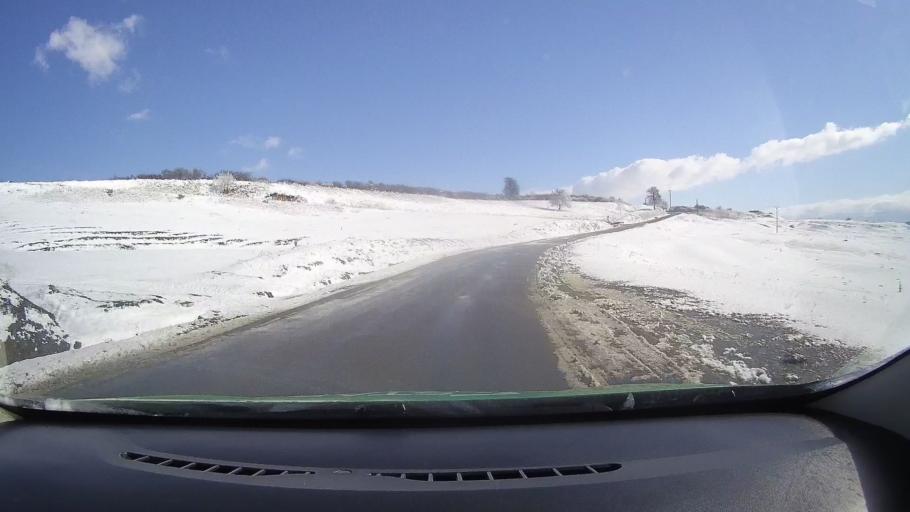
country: RO
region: Sibiu
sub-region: Comuna Rosia
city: Rosia
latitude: 45.8079
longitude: 24.2917
